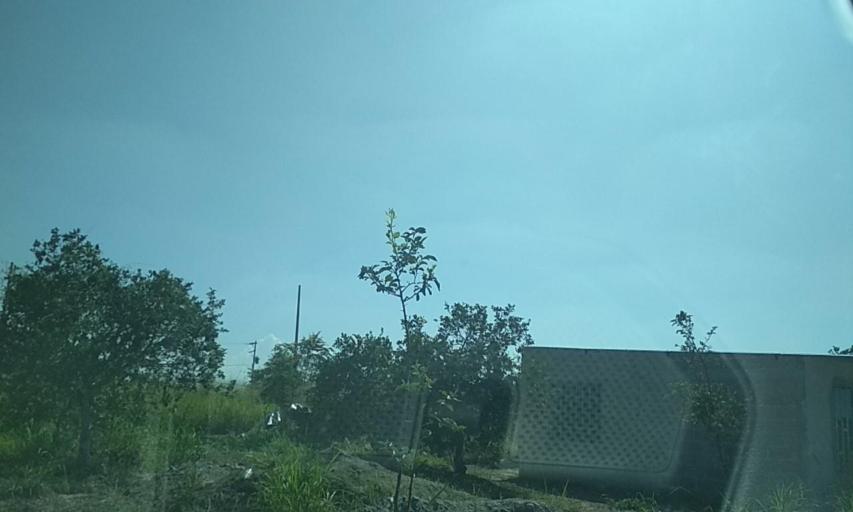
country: MX
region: Veracruz
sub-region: Martinez de la Torre
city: La Union Paso Largo
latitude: 20.1439
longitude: -97.0031
